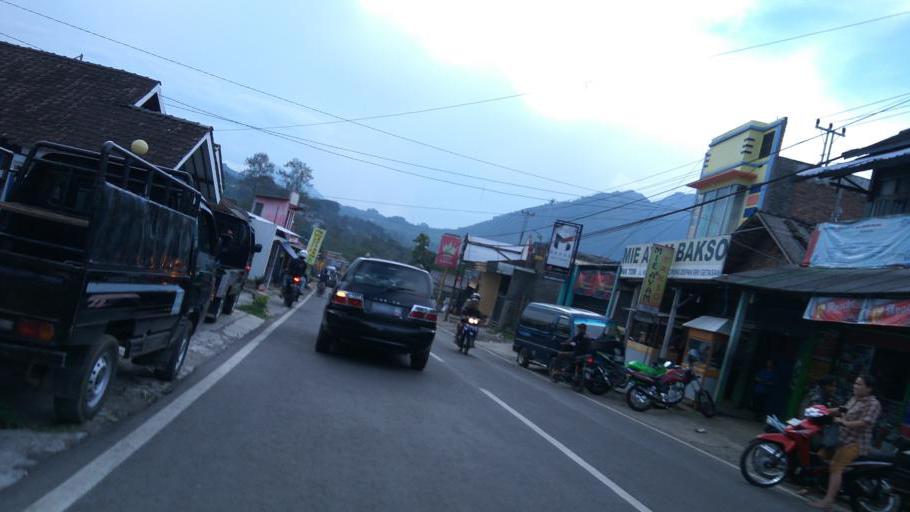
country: ID
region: Central Java
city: Gunung Kendil
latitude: -7.3752
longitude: 110.4368
